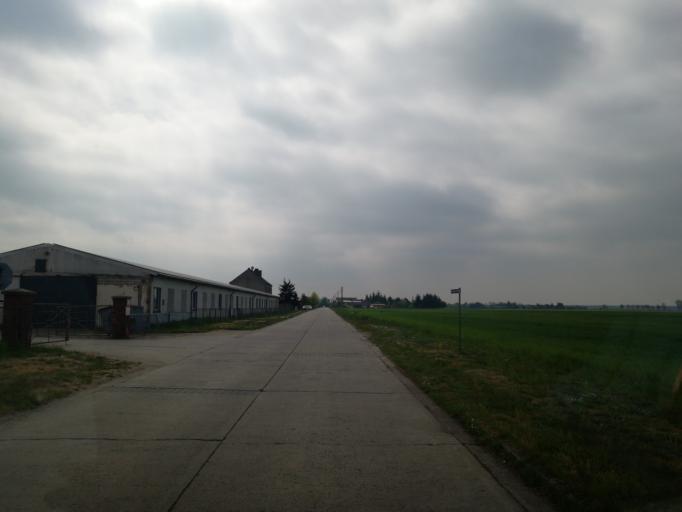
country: DE
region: Saxony
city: Beilrode
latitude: 51.6525
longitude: 13.1156
